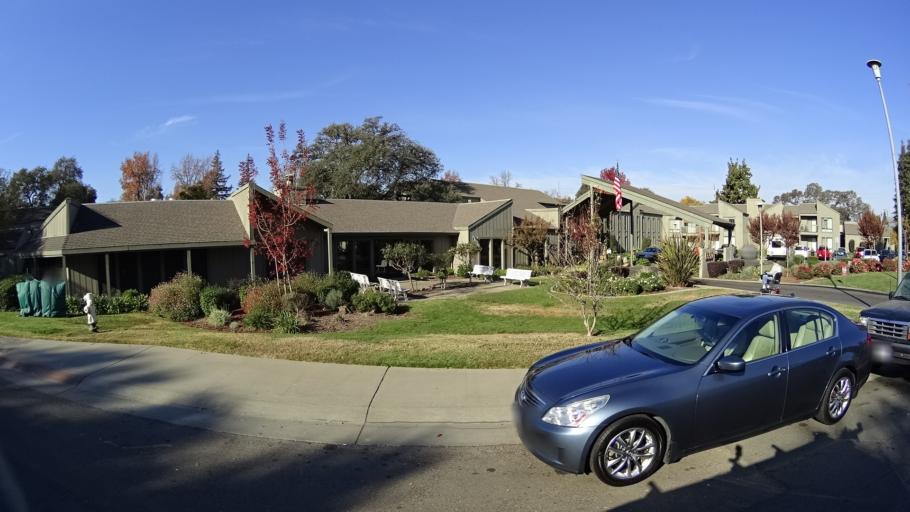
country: US
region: California
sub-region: Sacramento County
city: Citrus Heights
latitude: 38.6879
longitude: -121.3056
